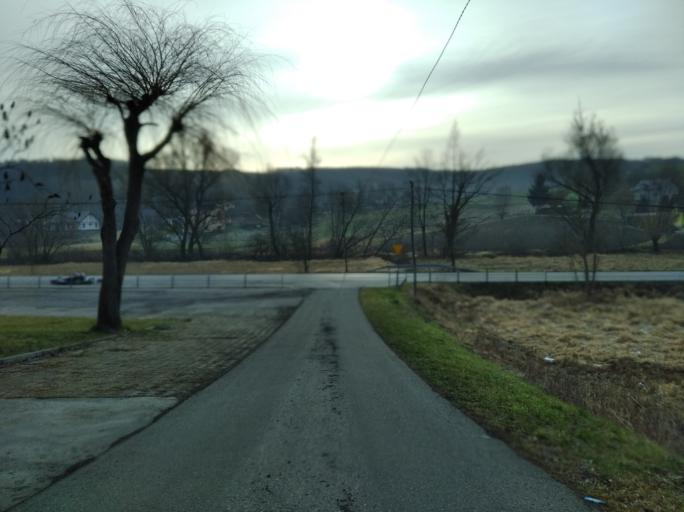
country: PL
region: Subcarpathian Voivodeship
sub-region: Powiat strzyzowski
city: Czudec
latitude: 49.9250
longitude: 21.8001
